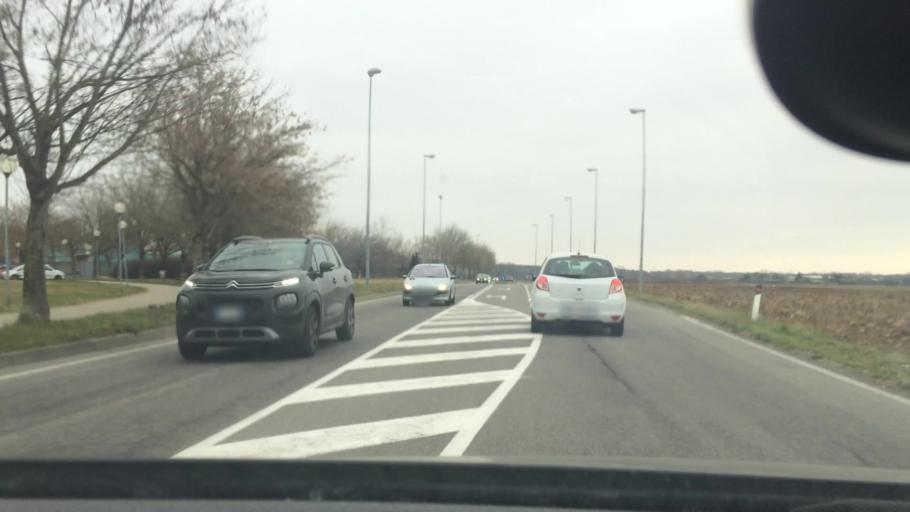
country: IT
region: Lombardy
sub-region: Citta metropolitana di Milano
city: Solaro
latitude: 45.6134
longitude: 9.0730
